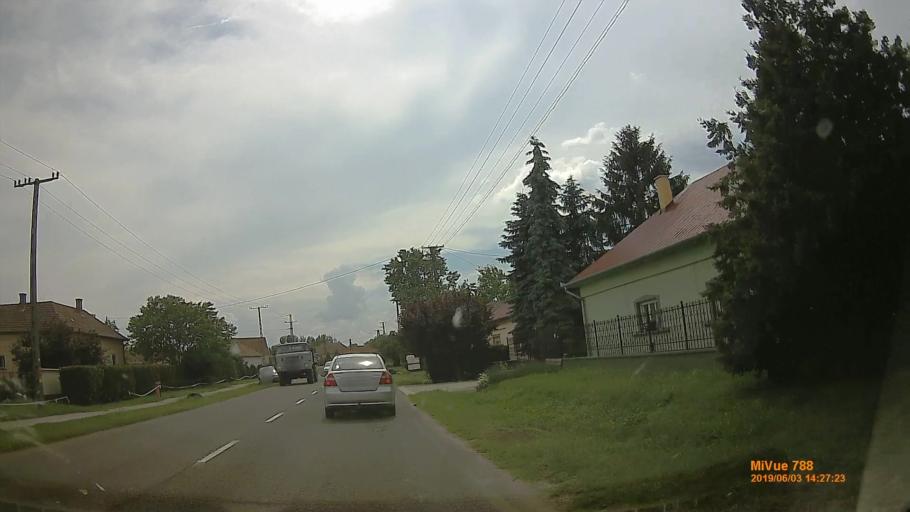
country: HU
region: Bacs-Kiskun
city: Tiszakecske
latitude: 46.9859
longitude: 20.1182
